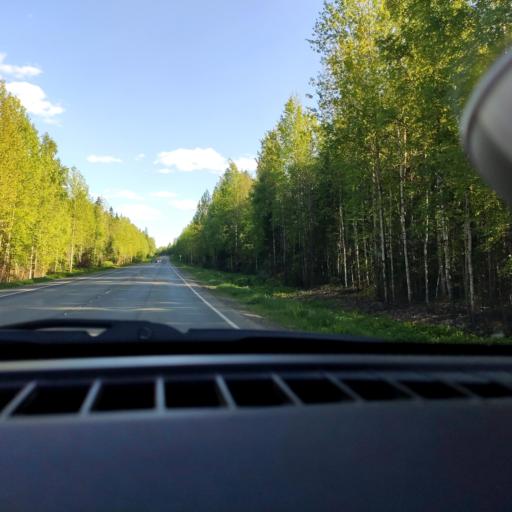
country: RU
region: Perm
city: Perm
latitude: 58.2318
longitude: 56.1617
